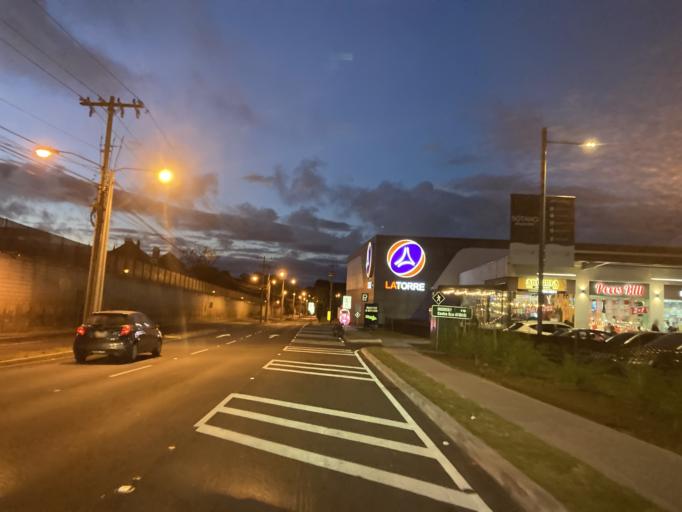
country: GT
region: Guatemala
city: Santa Catarina Pinula
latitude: 14.6056
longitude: -90.4688
